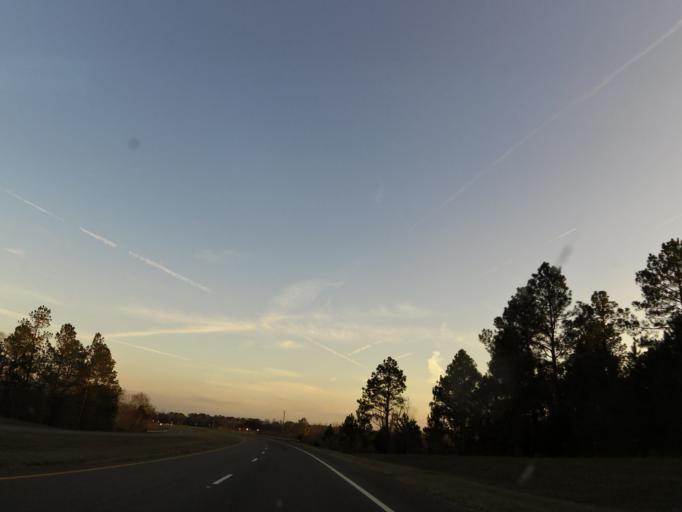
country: US
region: Georgia
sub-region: Lee County
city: Leesburg
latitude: 31.7267
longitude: -84.1821
